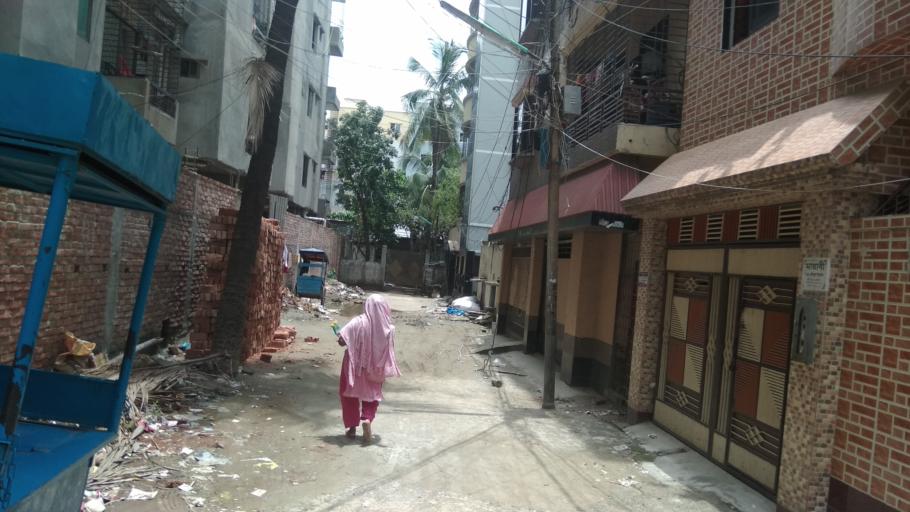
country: BD
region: Dhaka
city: Azimpur
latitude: 23.8127
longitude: 90.3713
